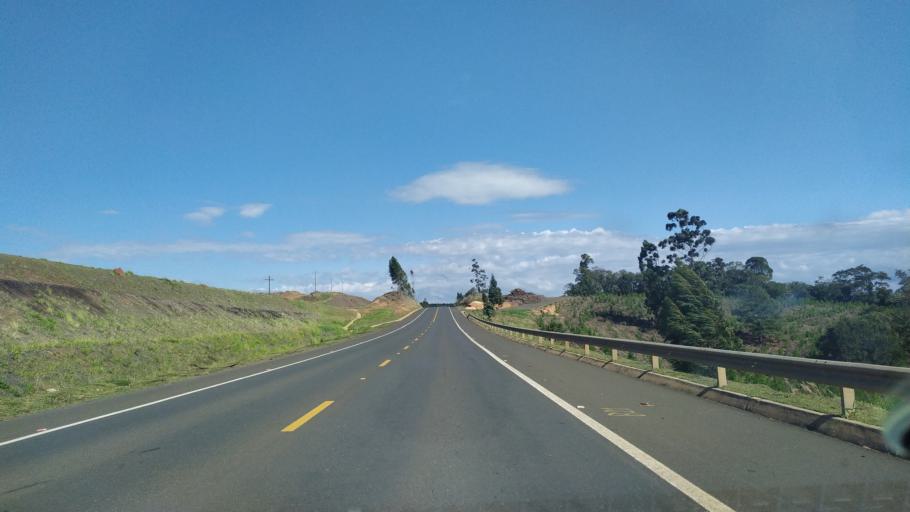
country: BR
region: Parana
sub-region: Ortigueira
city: Ortigueira
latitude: -24.2833
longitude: -50.8103
